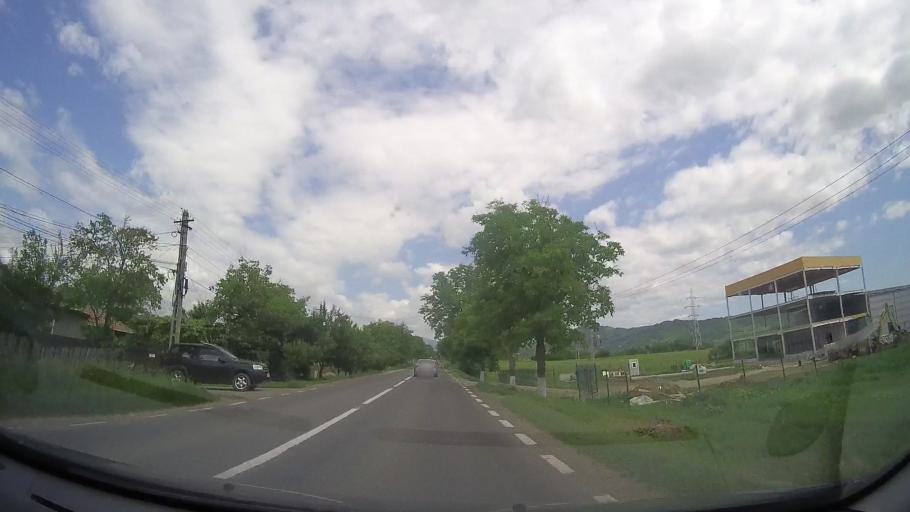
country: RO
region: Prahova
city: Drajna de Jos
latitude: 45.2359
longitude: 26.0291
